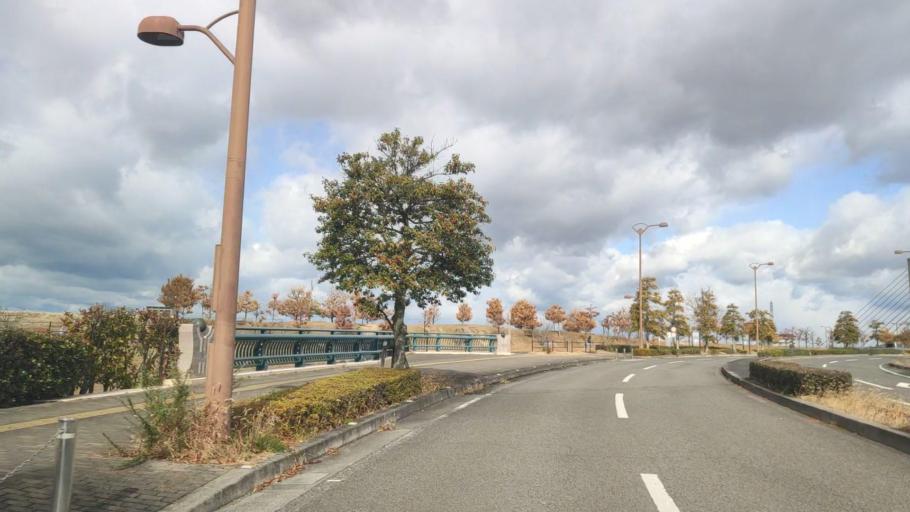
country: JP
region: Ehime
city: Masaki-cho
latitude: 33.8085
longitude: 132.7406
